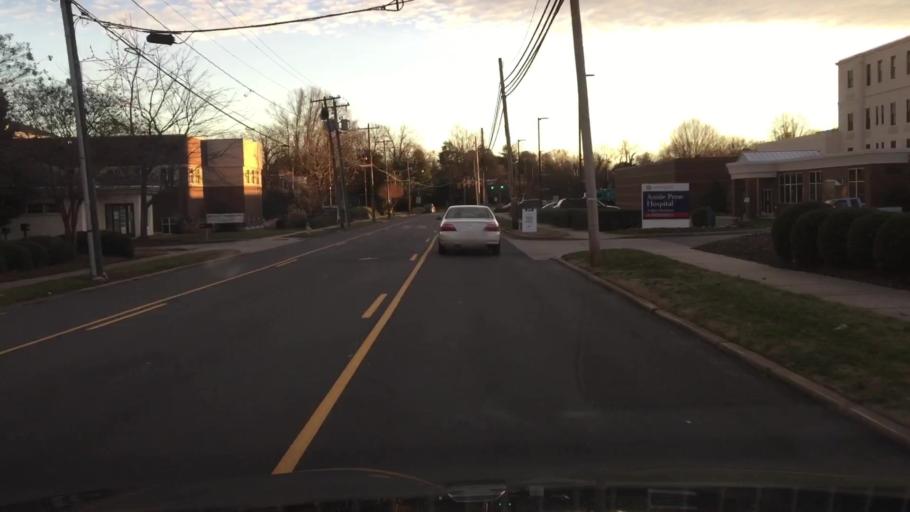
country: US
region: North Carolina
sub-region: Rockingham County
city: Reidsville
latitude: 36.3542
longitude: -79.6663
